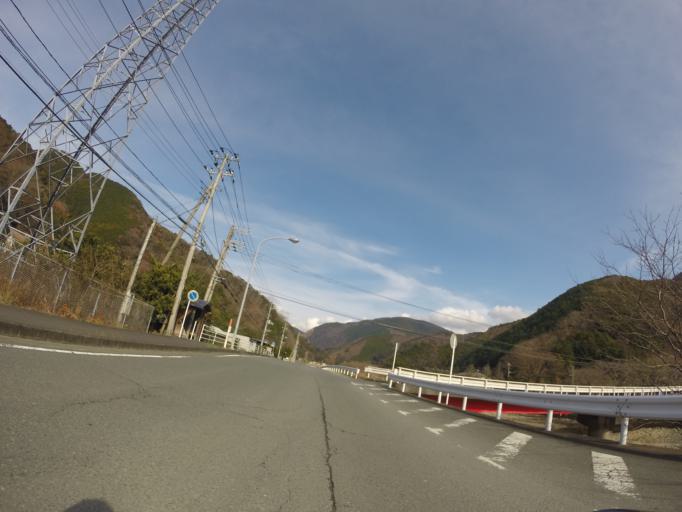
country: JP
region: Shizuoka
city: Heda
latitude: 34.7814
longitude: 138.7950
